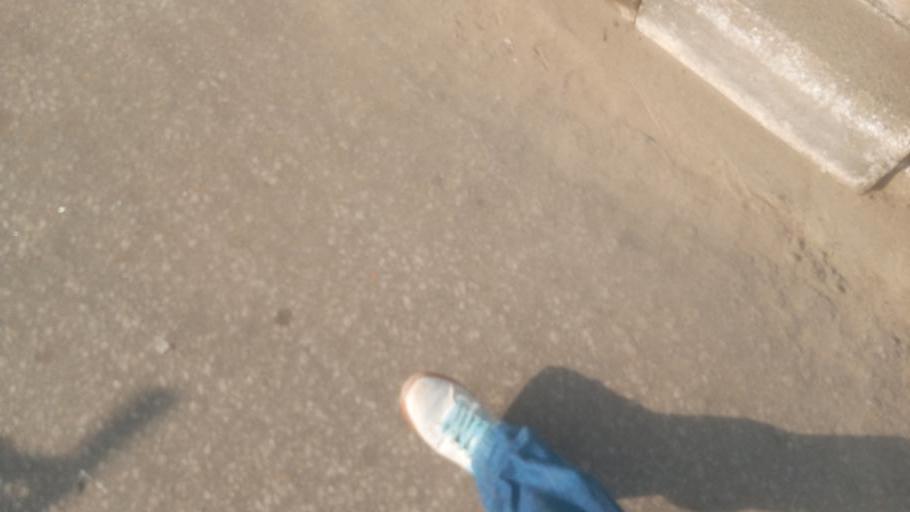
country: SL
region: Western Area
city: Freetown
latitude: 8.4757
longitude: -13.2432
